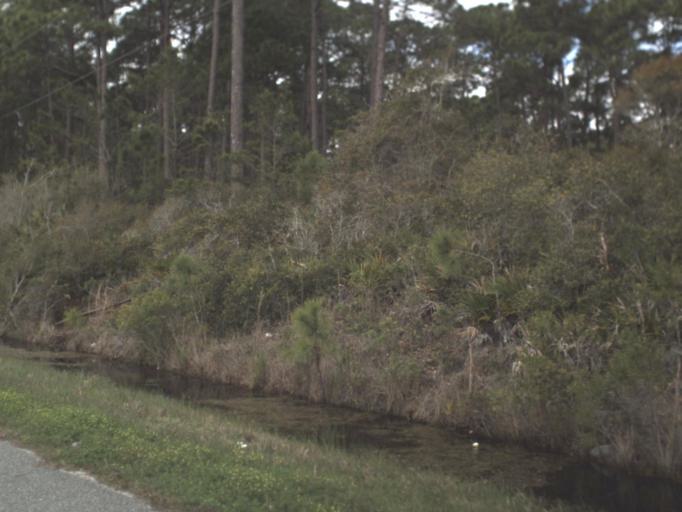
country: US
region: Florida
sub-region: Franklin County
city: Eastpoint
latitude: 29.7658
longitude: -84.8094
